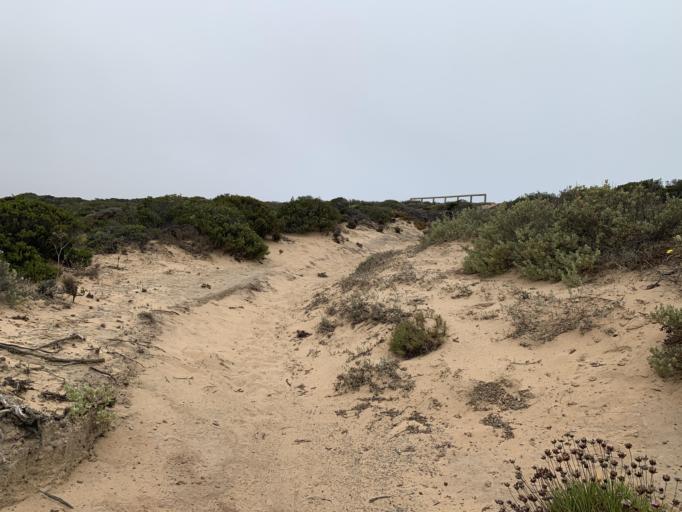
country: PT
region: Faro
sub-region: Aljezur
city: Aljezur
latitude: 37.3360
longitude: -8.8574
